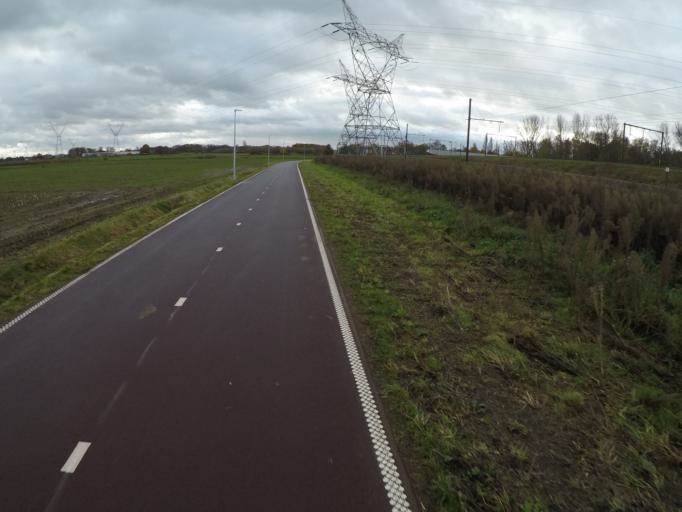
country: BE
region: Flanders
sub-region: Provincie Antwerpen
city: Hove
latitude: 51.1772
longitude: 4.4734
